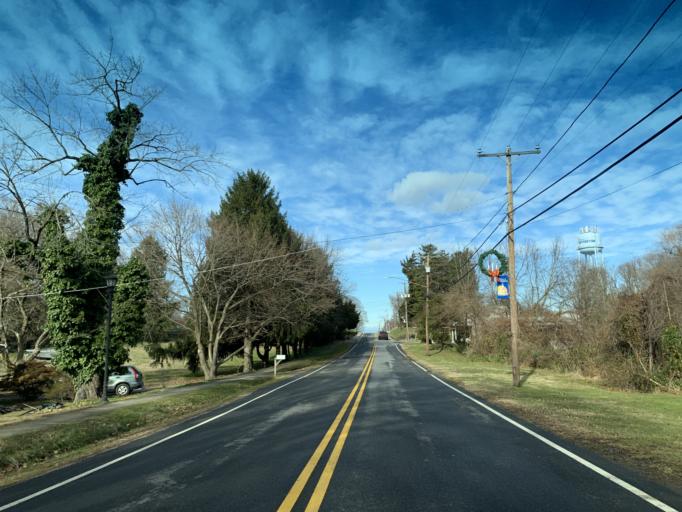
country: US
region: Maryland
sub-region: Harford County
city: Aberdeen Proving Ground
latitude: 39.3645
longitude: -76.0626
